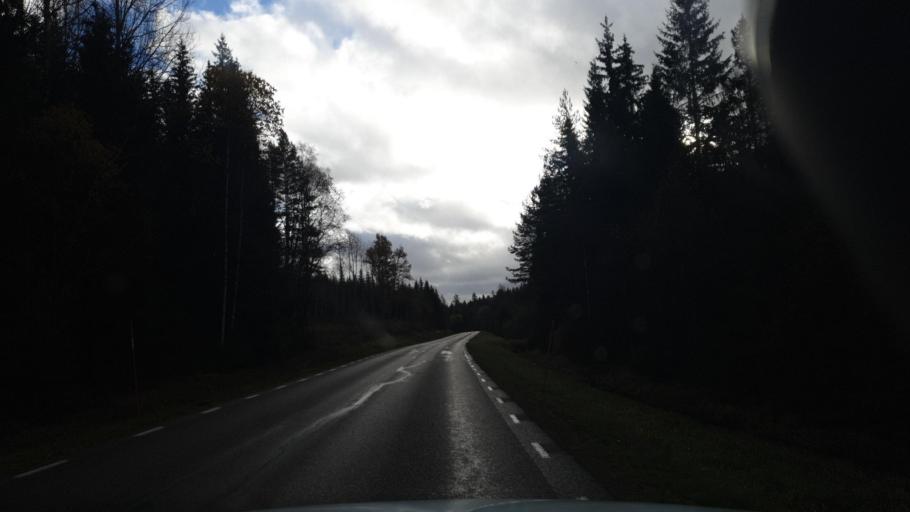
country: SE
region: Vaermland
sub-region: Grums Kommun
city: Slottsbron
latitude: 59.4580
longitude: 12.8362
